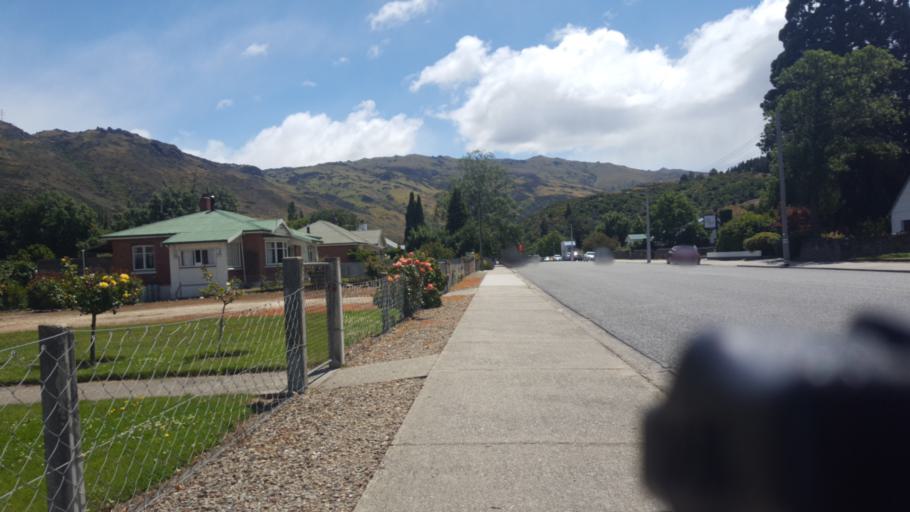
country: NZ
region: Otago
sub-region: Queenstown-Lakes District
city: Wanaka
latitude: -45.1887
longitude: 169.3188
